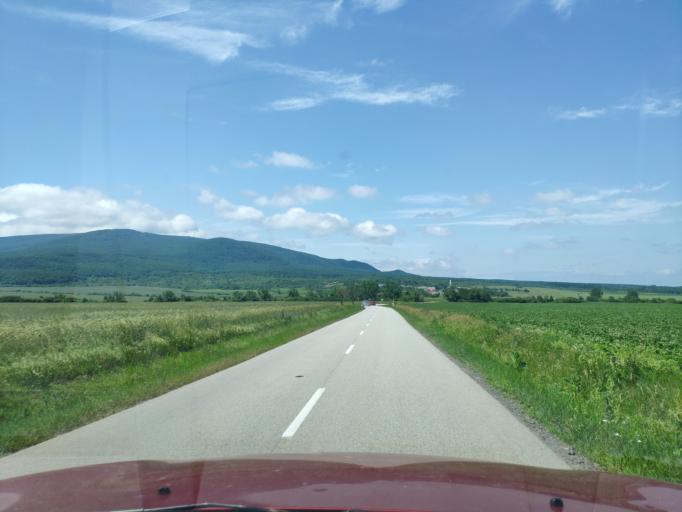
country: SK
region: Kosicky
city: Secovce
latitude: 48.7463
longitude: 21.6444
